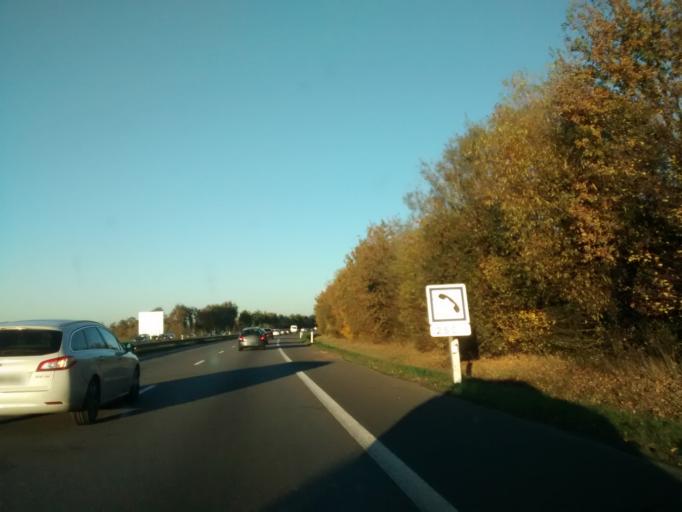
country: FR
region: Brittany
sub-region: Departement d'Ille-et-Vilaine
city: Montgermont
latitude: 48.1358
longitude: -1.7046
